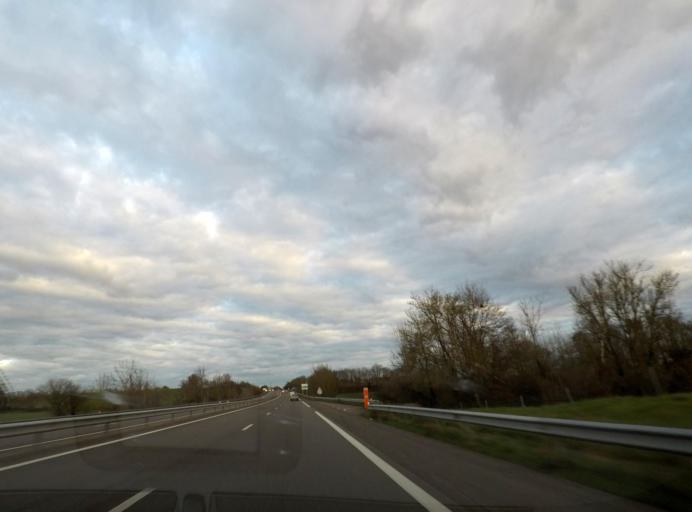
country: FR
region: Rhone-Alpes
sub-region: Departement de l'Ain
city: Mezeriat
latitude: 46.2711
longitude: 5.0250
